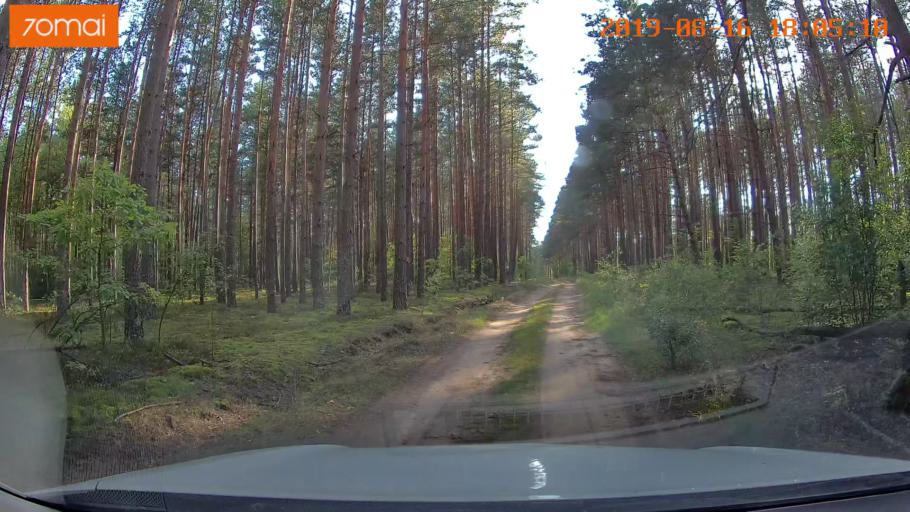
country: BY
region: Mogilev
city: Asipovichy
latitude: 53.2177
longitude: 28.6536
